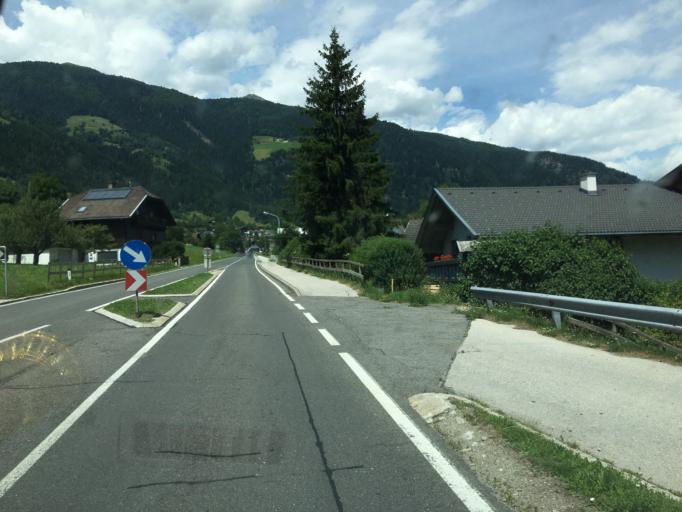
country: AT
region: Carinthia
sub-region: Politischer Bezirk Spittal an der Drau
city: Winklern
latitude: 46.8655
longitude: 12.8825
